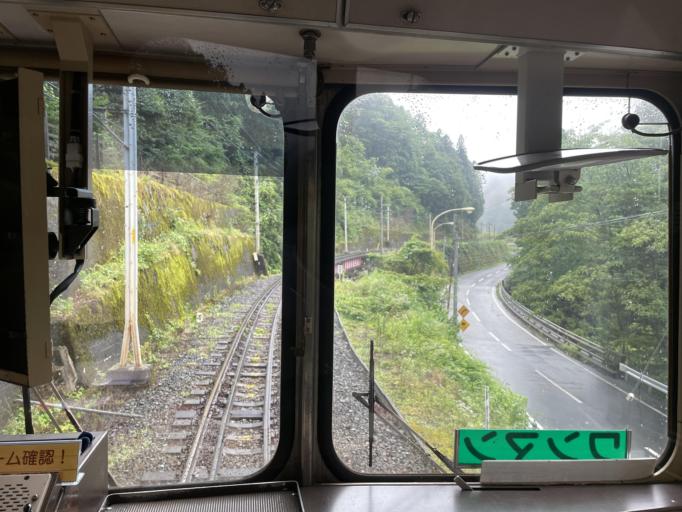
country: JP
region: Saitama
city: Chichibu
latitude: 35.9566
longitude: 139.0042
